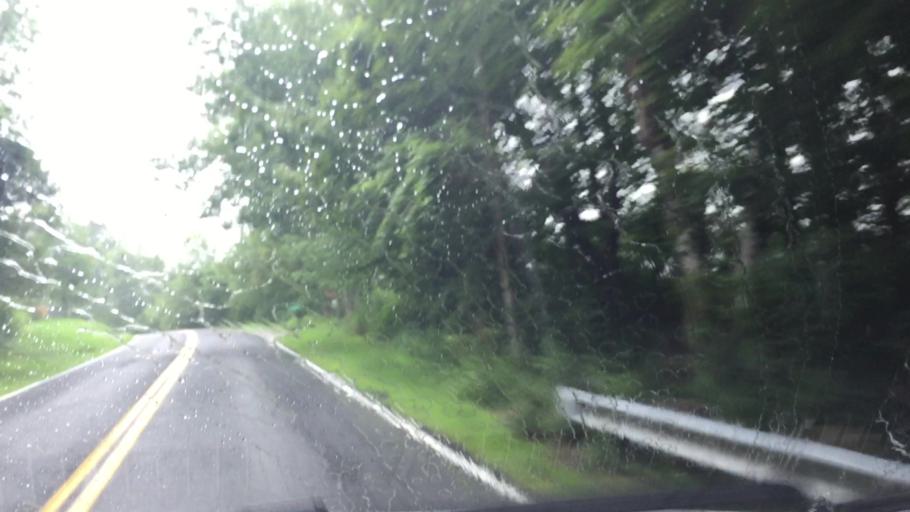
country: US
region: Massachusetts
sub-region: Berkshire County
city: Housatonic
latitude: 42.2957
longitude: -73.4033
